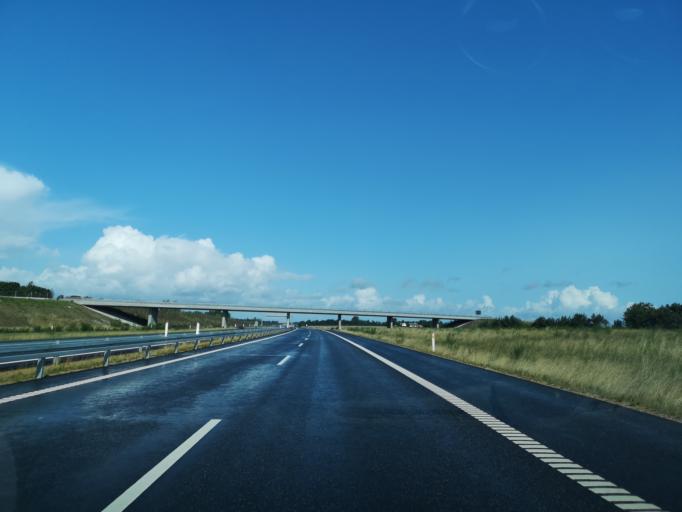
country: DK
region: Central Jutland
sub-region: Herning Kommune
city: Snejbjerg
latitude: 56.1960
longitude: 8.8839
